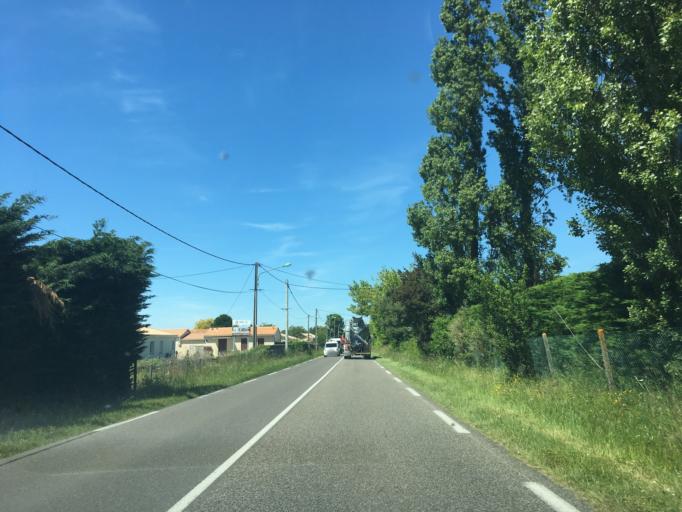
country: FR
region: Aquitaine
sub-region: Departement de la Gironde
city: Listrac-Medoc
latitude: 45.0790
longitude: -0.7947
